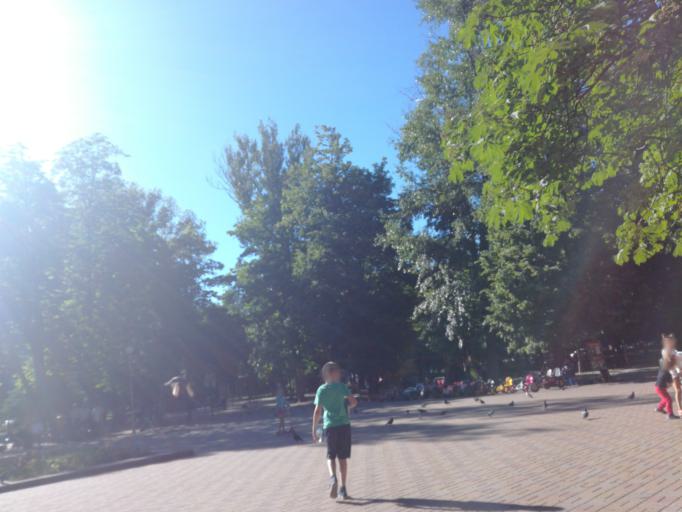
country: RU
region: Kursk
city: Kursk
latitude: 51.7452
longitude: 36.1889
